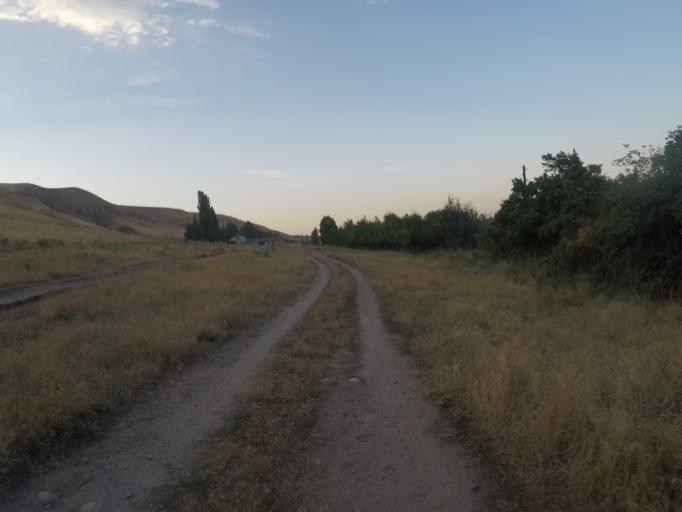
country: KG
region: Chuy
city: Bishkek
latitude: 42.7709
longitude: 74.6394
